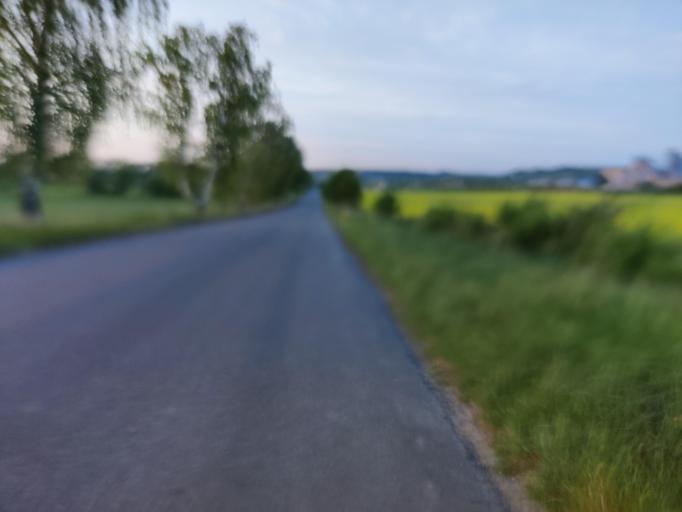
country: DE
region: Saxony-Anhalt
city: Karsdorf
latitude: 51.2643
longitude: 11.6469
